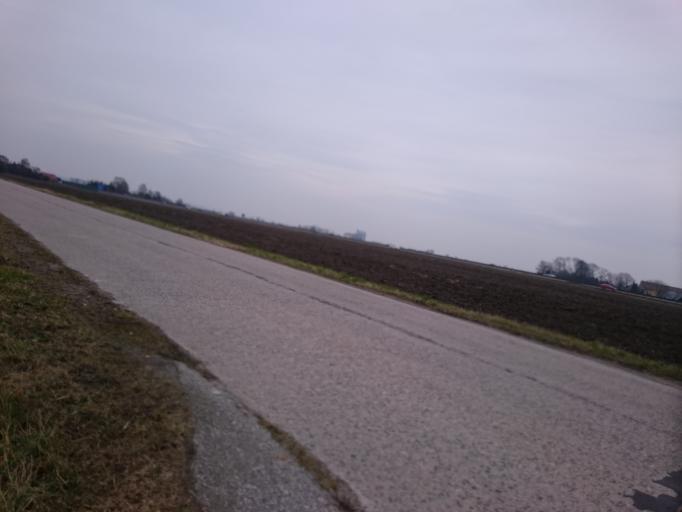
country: SE
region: Skane
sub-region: Staffanstorps Kommun
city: Hjaerup
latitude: 55.6715
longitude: 13.1659
